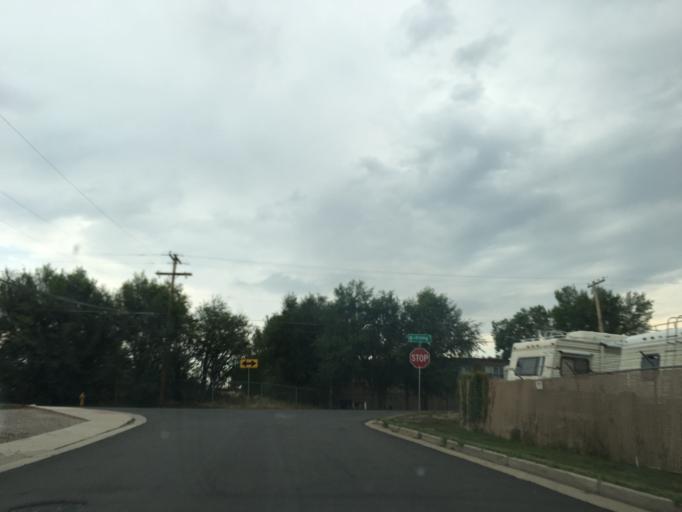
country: US
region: Colorado
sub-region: Arapahoe County
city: Sheridan
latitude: 39.6559
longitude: -105.0303
